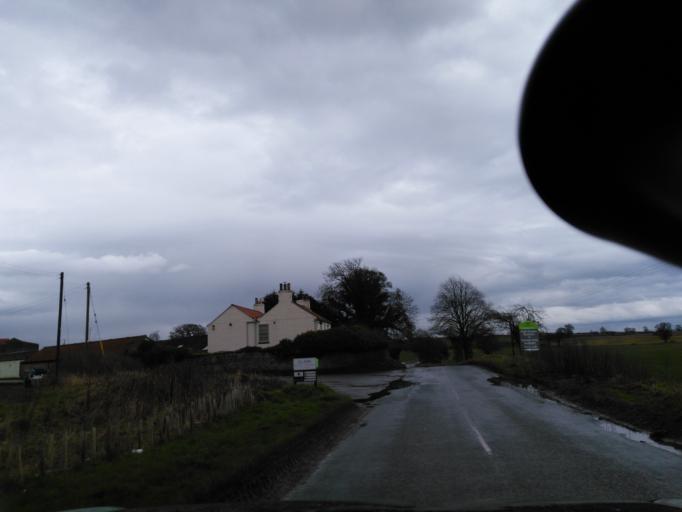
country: GB
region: England
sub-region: North Yorkshire
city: Ripon
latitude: 54.1430
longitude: -1.4652
